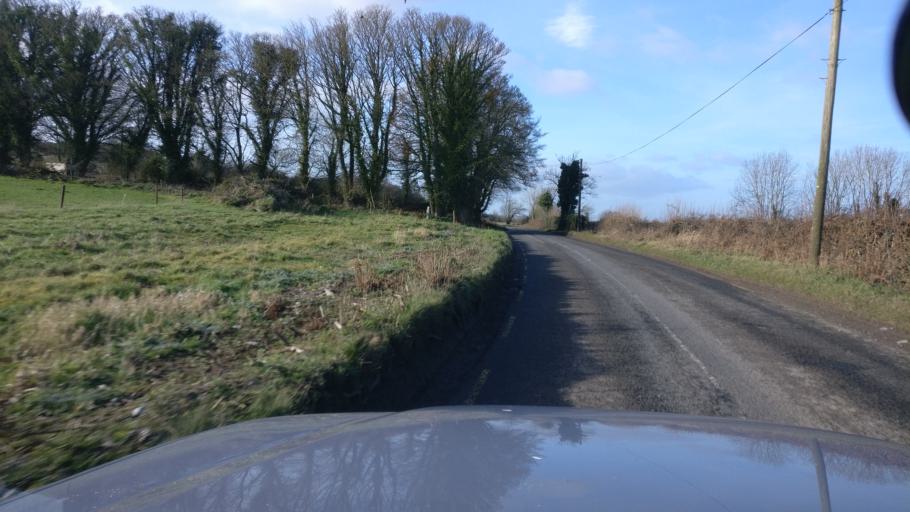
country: IE
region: Leinster
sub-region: Laois
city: Portlaoise
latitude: 53.0086
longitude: -7.2352
